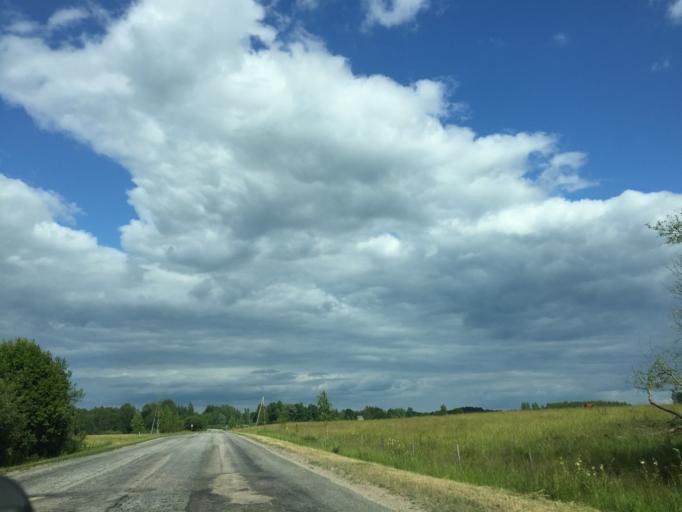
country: LV
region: Skriveri
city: Skriveri
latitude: 56.8043
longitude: 25.0902
